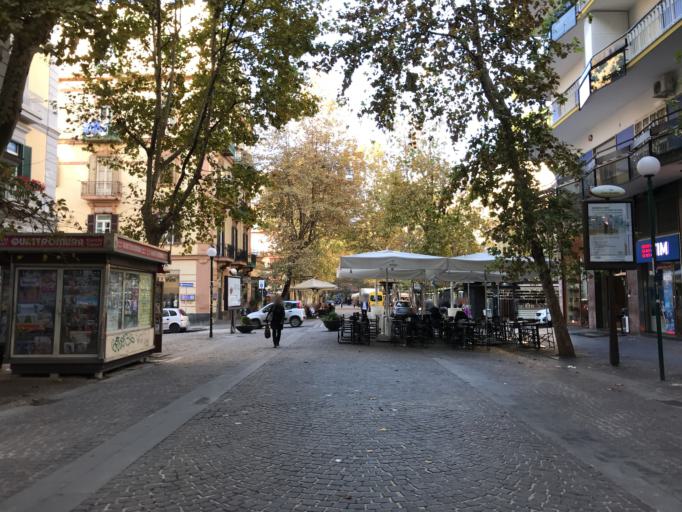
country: IT
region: Campania
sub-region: Provincia di Napoli
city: Napoli
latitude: 40.8449
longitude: 14.2280
